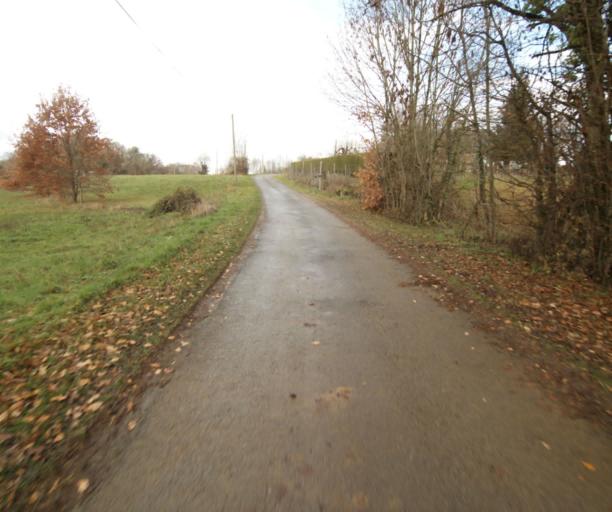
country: FR
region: Limousin
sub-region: Departement de la Correze
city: Sainte-Fereole
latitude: 45.2664
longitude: 1.6018
